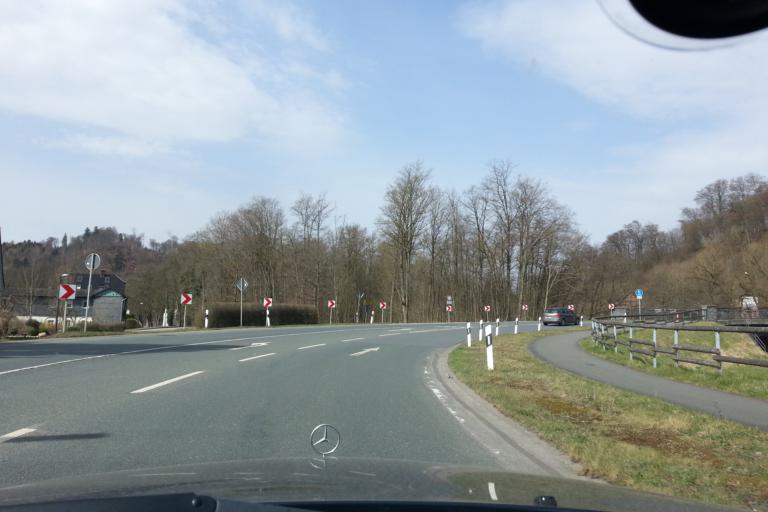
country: DE
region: North Rhine-Westphalia
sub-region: Regierungsbezirk Arnsberg
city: Meschede
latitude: 51.3489
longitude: 8.2614
